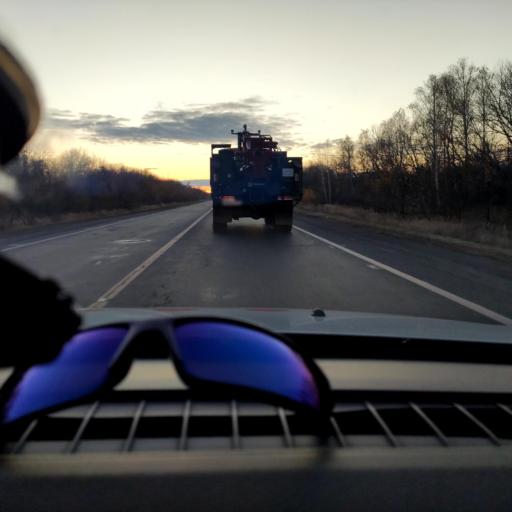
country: RU
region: Samara
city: Novokuybyshevsk
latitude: 52.9890
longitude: 49.8519
